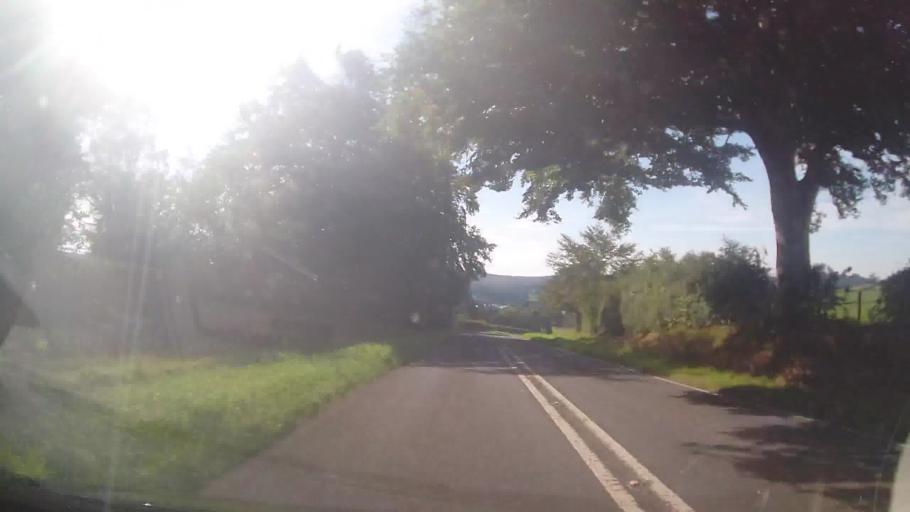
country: GB
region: Wales
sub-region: Sir Powys
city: Rhayader
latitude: 52.3036
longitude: -3.4912
